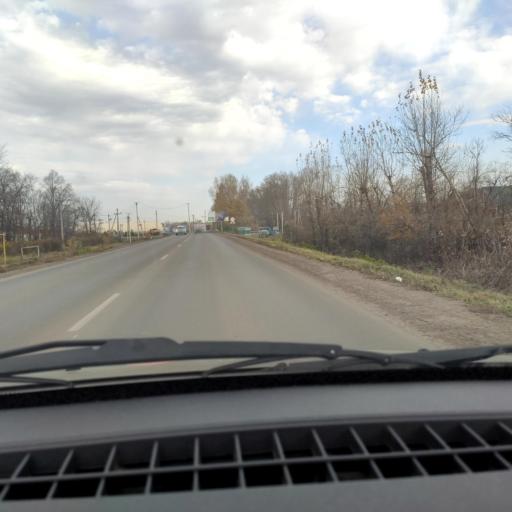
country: RU
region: Bashkortostan
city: Ufa
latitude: 54.6291
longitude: 55.9188
